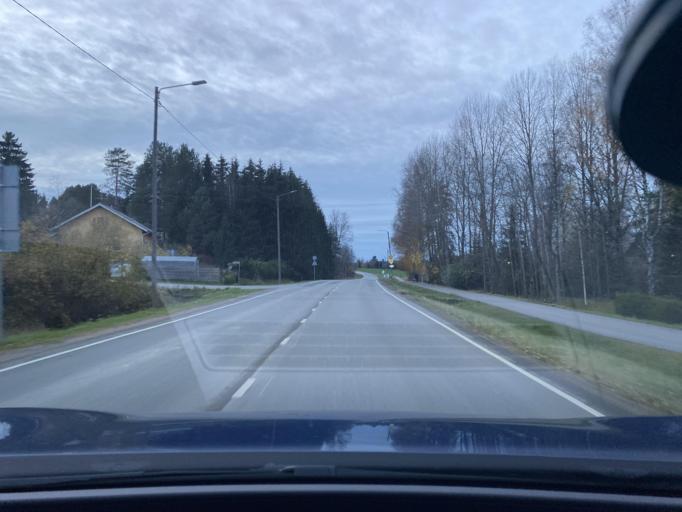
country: FI
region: Uusimaa
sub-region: Helsinki
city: Saukkola
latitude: 60.3805
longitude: 23.9563
